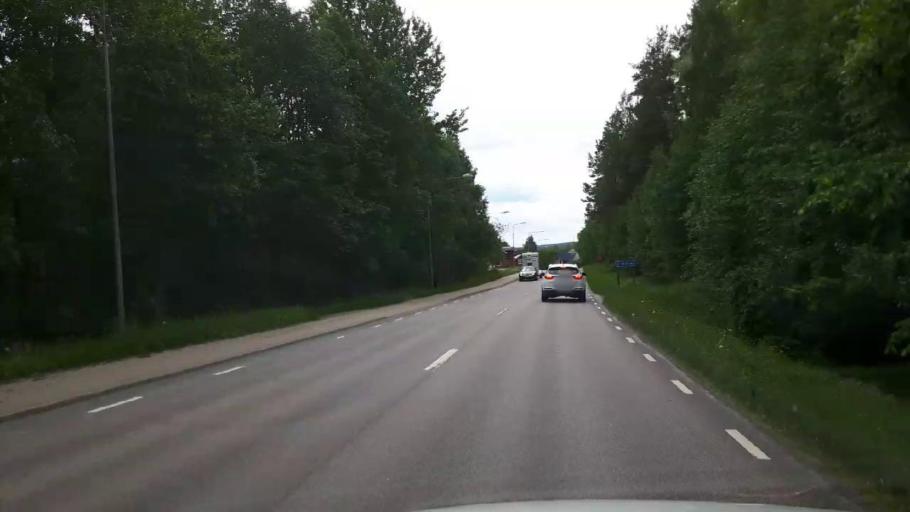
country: SE
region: Vaestmanland
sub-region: Norbergs Kommun
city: Norberg
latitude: 60.0793
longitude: 15.9328
